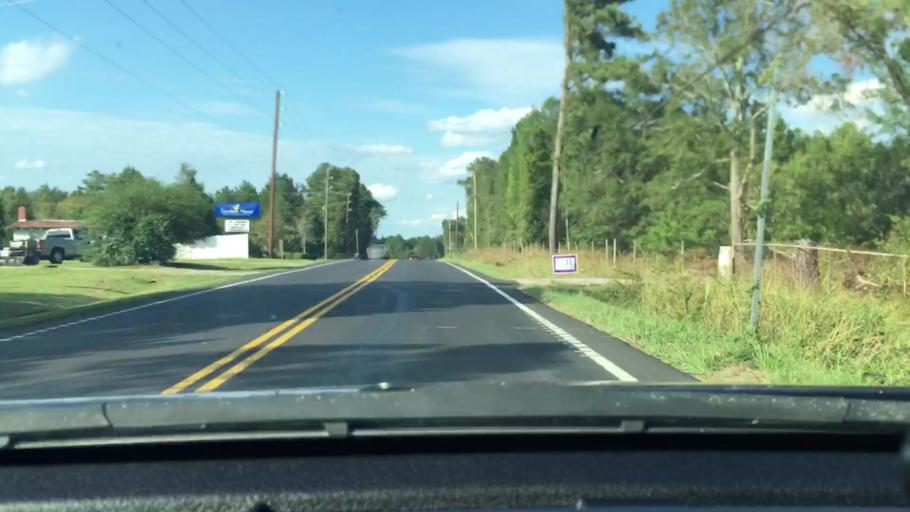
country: US
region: South Carolina
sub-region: Lexington County
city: Irmo
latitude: 34.1011
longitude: -81.1603
